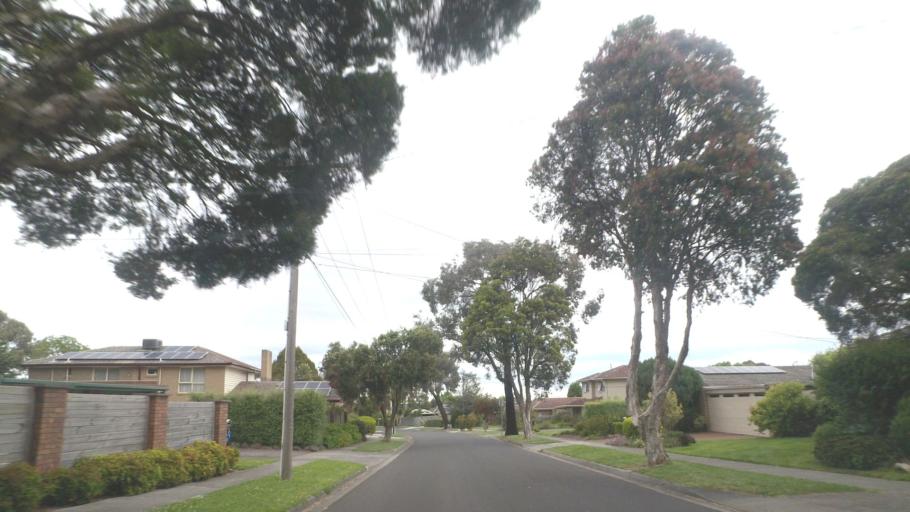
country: AU
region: Victoria
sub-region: Knox
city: Bayswater
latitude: -37.8503
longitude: 145.2521
